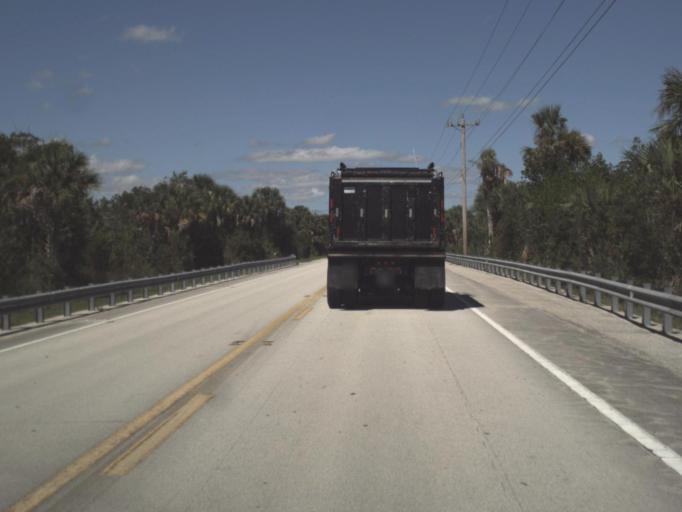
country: US
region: Florida
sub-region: Collier County
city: Marco
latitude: 25.9830
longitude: -81.5645
